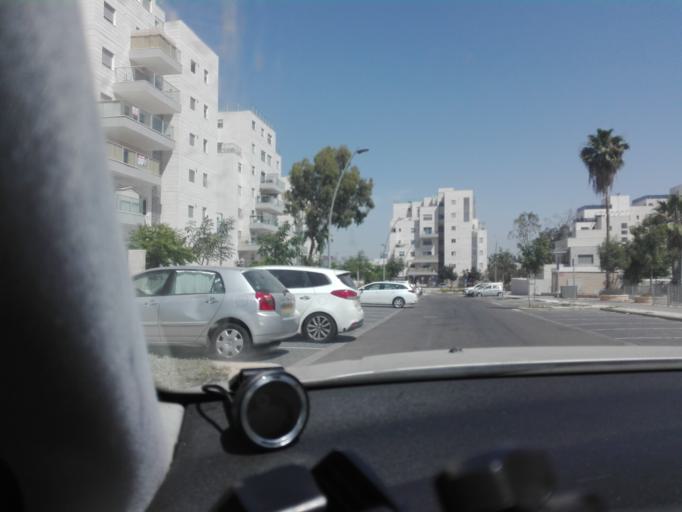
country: IL
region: Central District
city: Bene 'Ayish
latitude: 31.7237
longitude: 34.7436
